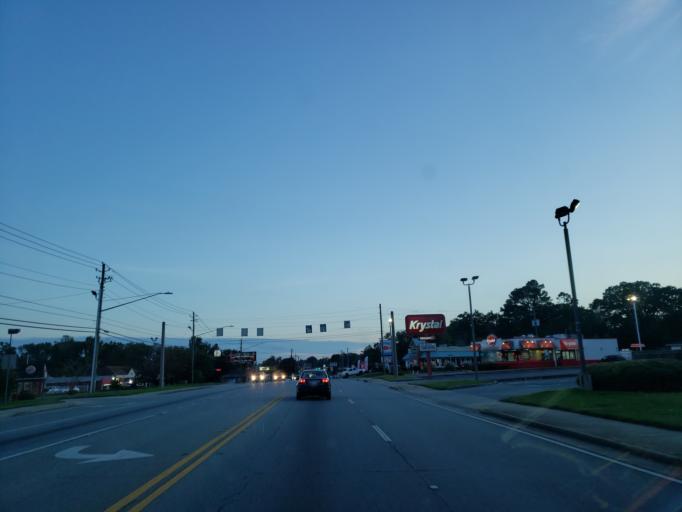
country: US
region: Georgia
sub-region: Polk County
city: Cedartown
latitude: 34.0238
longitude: -85.2506
